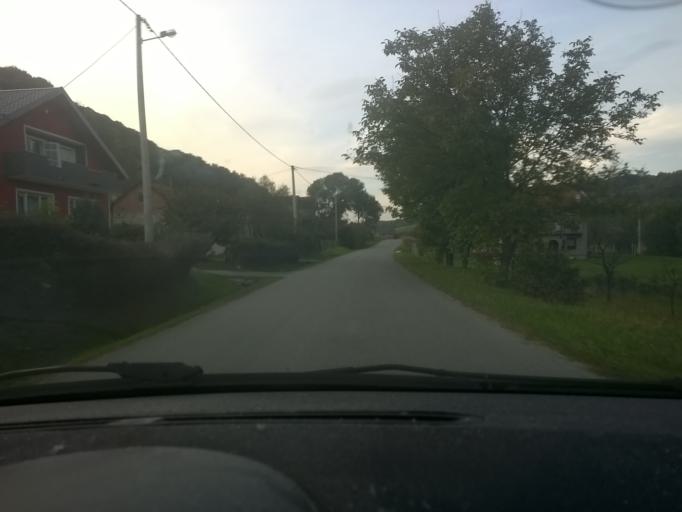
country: HR
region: Krapinsko-Zagorska
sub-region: Grad Krapina
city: Krapina
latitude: 46.1186
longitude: 15.8588
